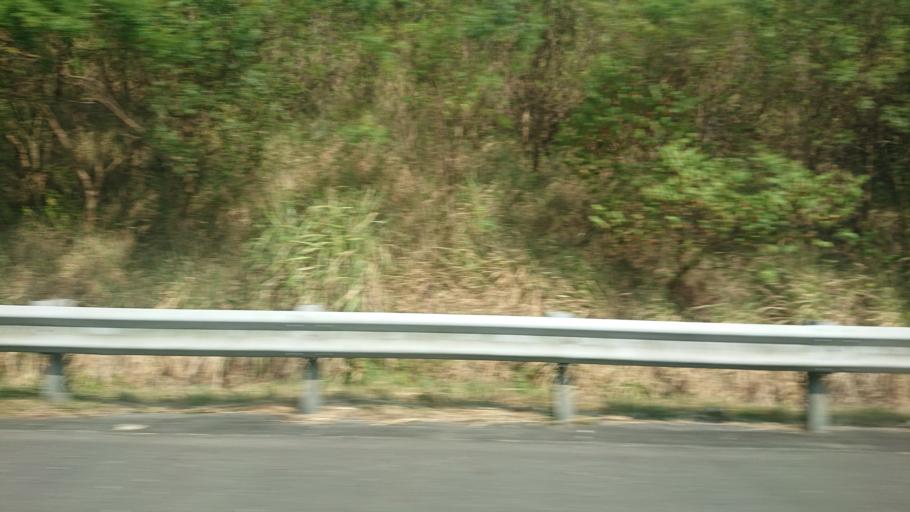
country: TW
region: Taiwan
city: Lugu
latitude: 23.7778
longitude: 120.6867
